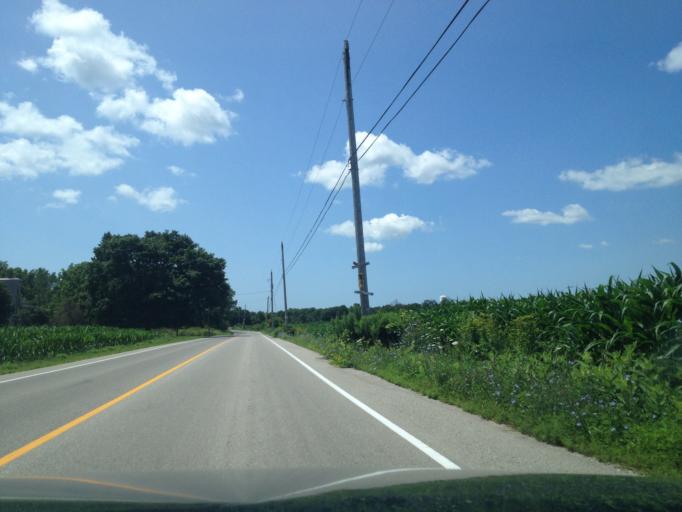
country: CA
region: Ontario
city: Norfolk County
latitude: 42.6371
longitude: -80.4391
